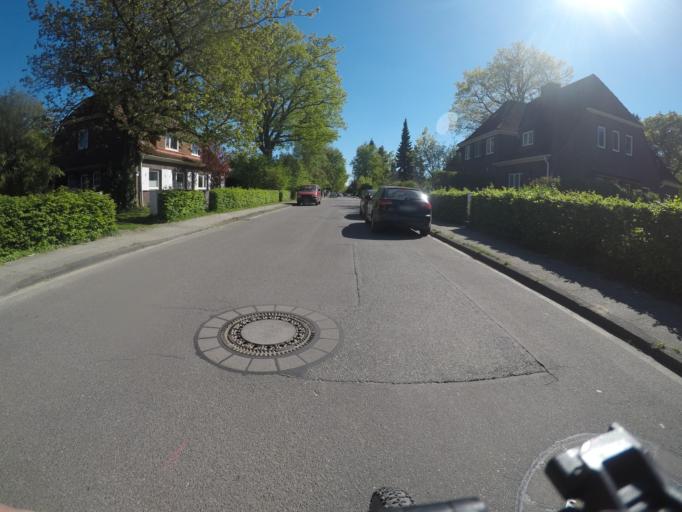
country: DE
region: Hamburg
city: Farmsen-Berne
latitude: 53.6257
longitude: 10.1223
